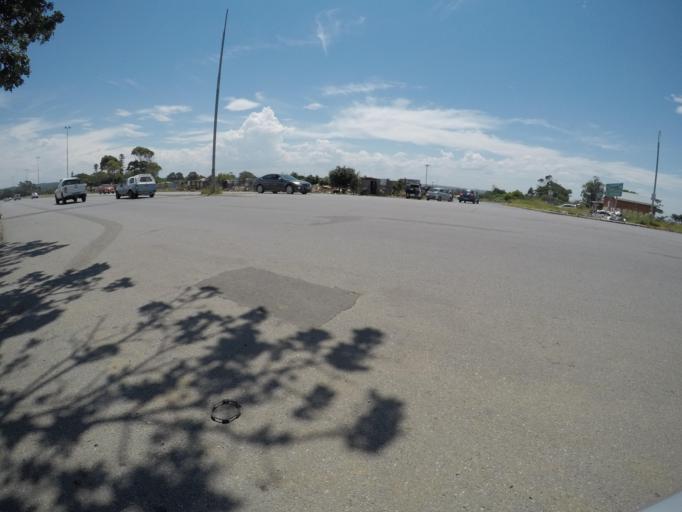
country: ZA
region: Eastern Cape
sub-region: Buffalo City Metropolitan Municipality
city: East London
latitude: -33.0353
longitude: 27.8450
